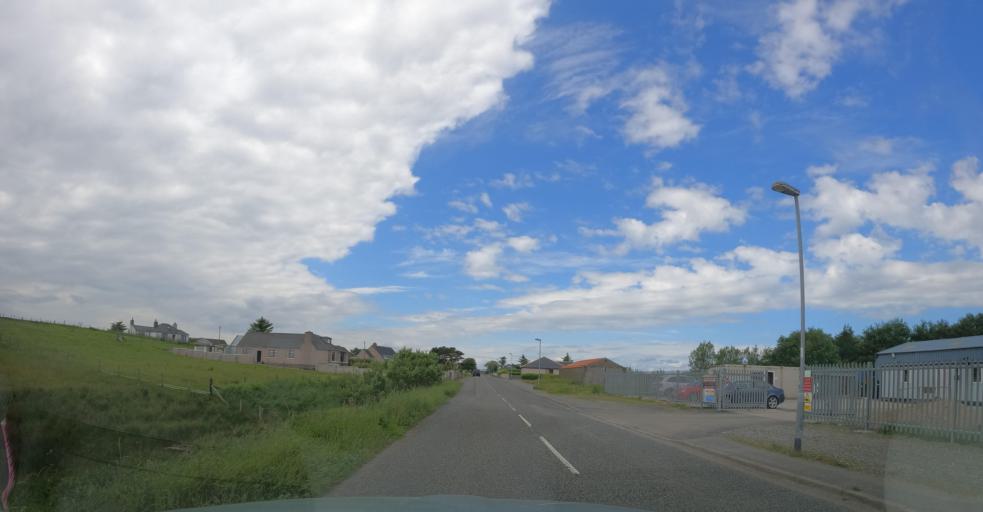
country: GB
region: Scotland
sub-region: Eilean Siar
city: Isle of Lewis
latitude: 58.2752
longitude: -6.3046
